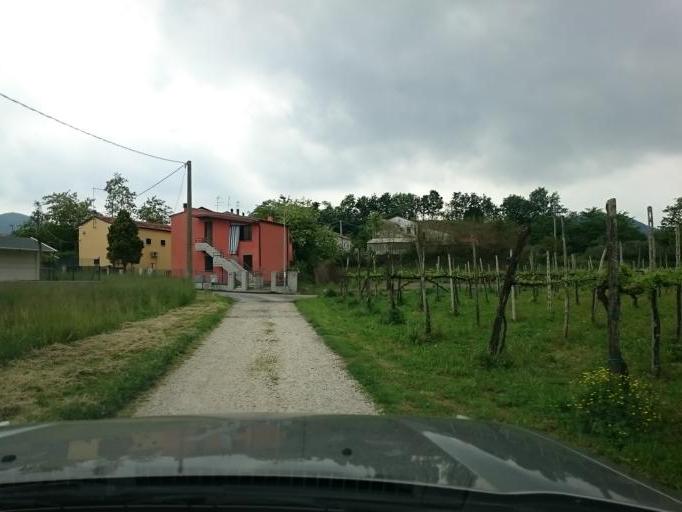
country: IT
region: Veneto
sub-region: Provincia di Padova
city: Battaglia Terme
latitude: 45.2773
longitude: 11.7602
